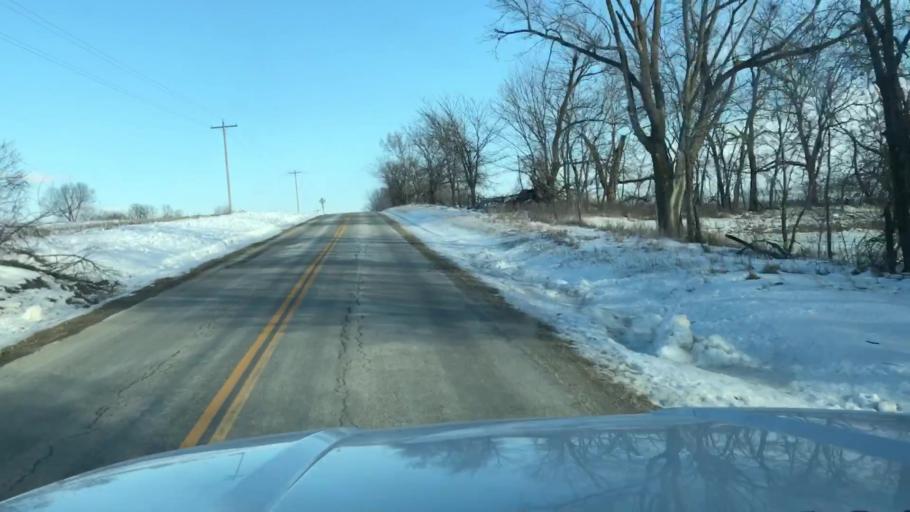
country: US
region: Missouri
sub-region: Holt County
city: Oregon
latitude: 40.1008
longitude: -95.0174
